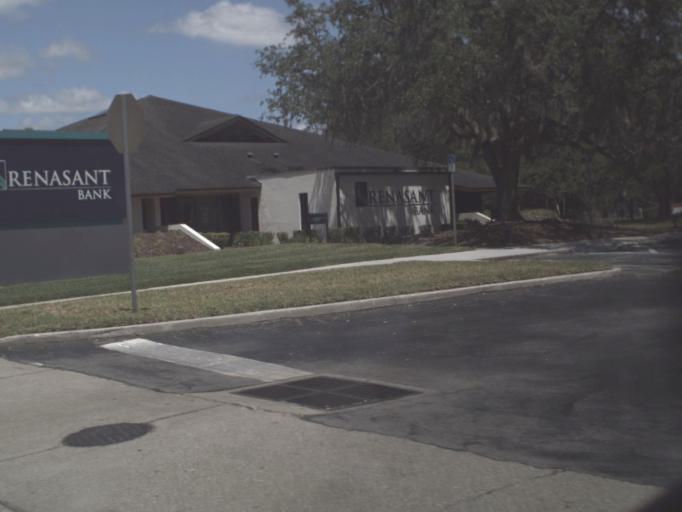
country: US
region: Florida
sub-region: Marion County
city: Ocala
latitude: 29.1870
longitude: -82.1192
